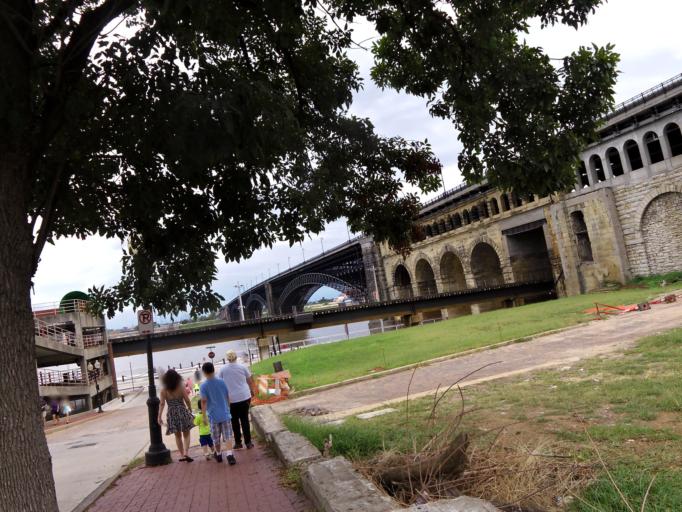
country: US
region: Missouri
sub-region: City of Saint Louis
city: St. Louis
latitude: 38.6298
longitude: -90.1830
